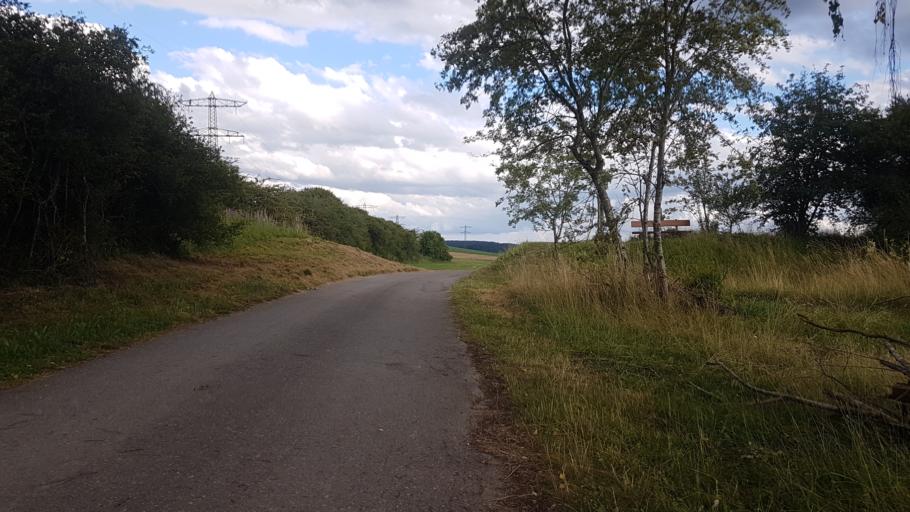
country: DE
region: Baden-Wuerttemberg
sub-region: Freiburg Region
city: Braunlingen
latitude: 47.9845
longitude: 8.4257
